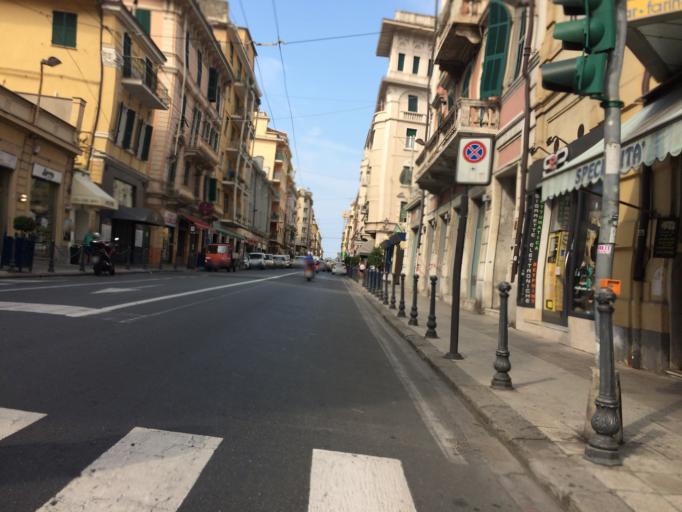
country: IT
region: Liguria
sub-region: Provincia di Imperia
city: San Remo
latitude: 43.8172
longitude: 7.7787
